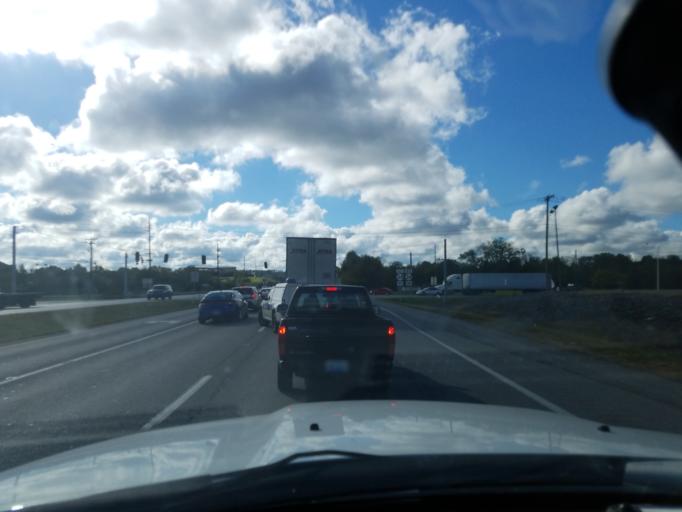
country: US
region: Kentucky
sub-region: Boyle County
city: Danville
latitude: 37.6297
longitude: -84.7982
